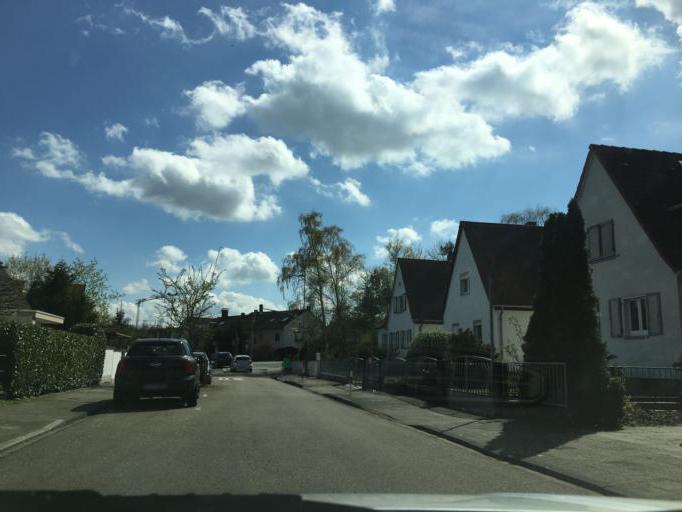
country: DE
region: Hesse
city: Heusenstamm
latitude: 50.0547
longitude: 8.8059
